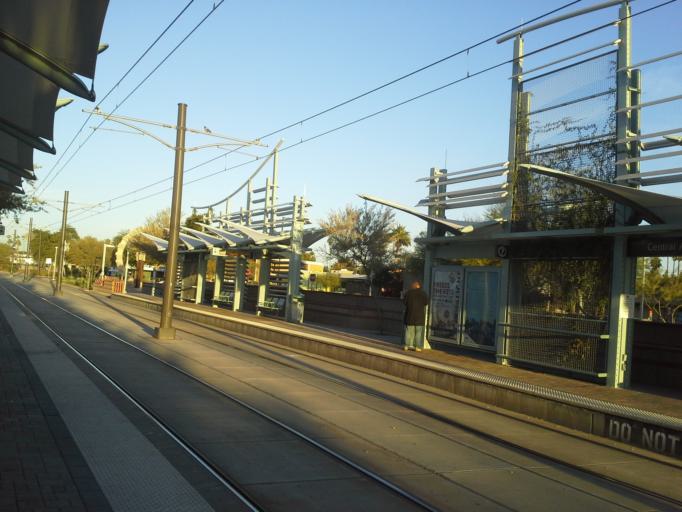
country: US
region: Arizona
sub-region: Maricopa County
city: Phoenix
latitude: 33.5086
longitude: -112.0753
